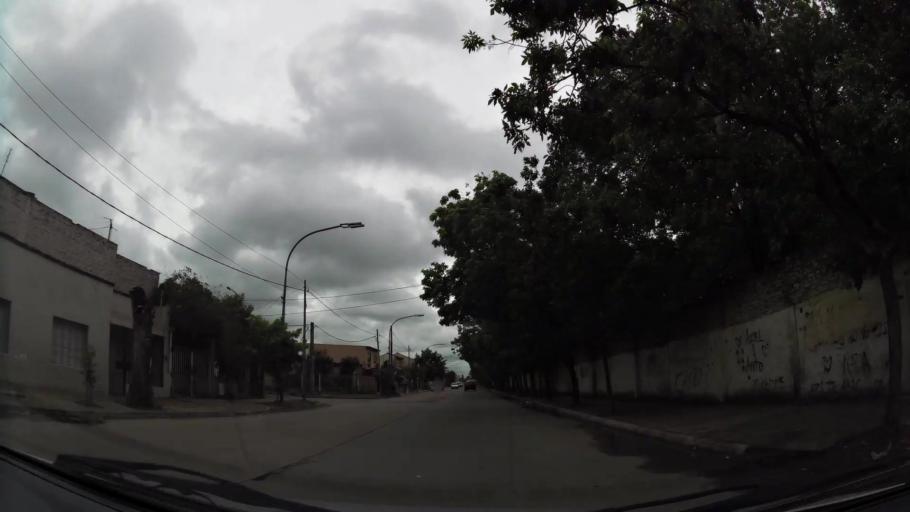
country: AR
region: Buenos Aires
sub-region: Partido de Lanus
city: Lanus
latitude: -34.7326
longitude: -58.3745
